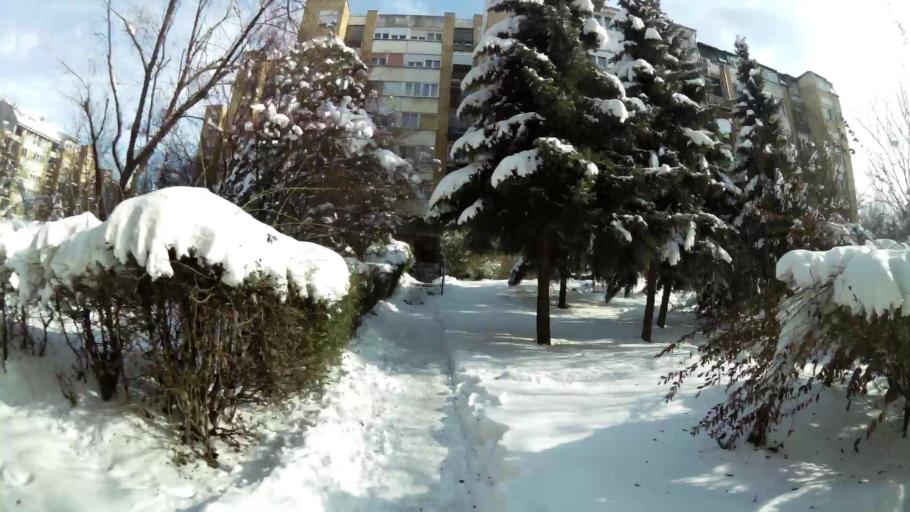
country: RS
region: Central Serbia
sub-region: Belgrade
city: Zvezdara
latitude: 44.7878
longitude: 20.5358
